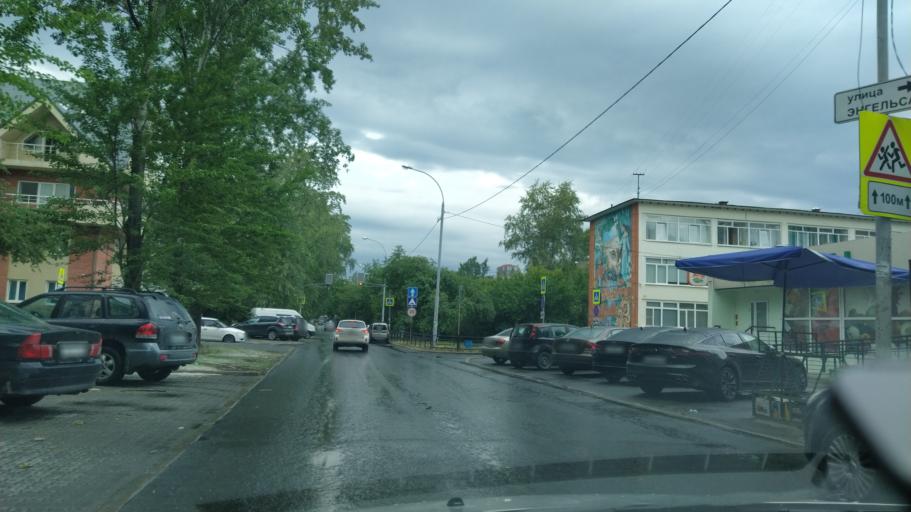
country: RU
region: Sverdlovsk
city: Yekaterinburg
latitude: 56.8330
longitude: 60.6287
